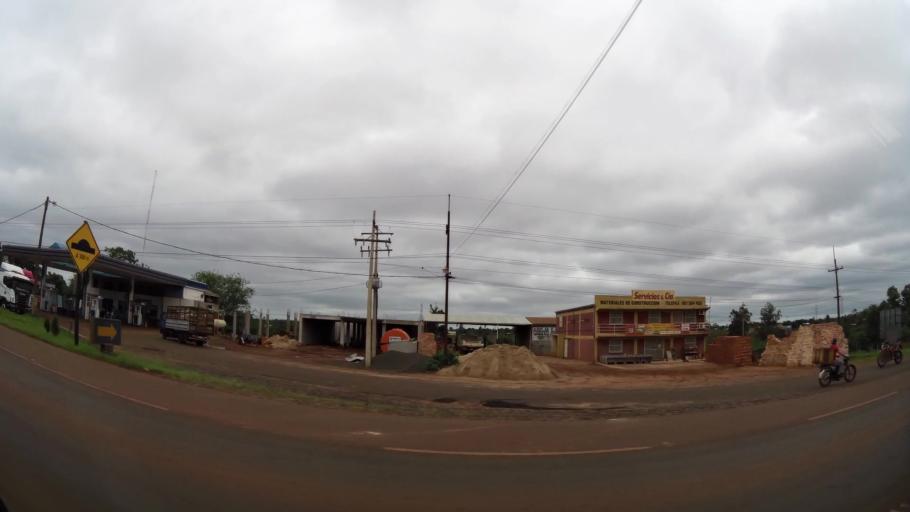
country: PY
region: Alto Parana
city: Presidente Franco
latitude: -25.4896
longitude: -54.7954
